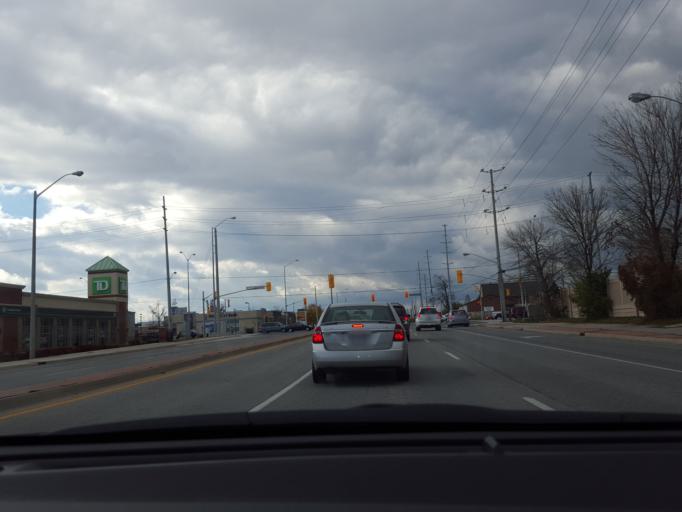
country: CA
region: Ontario
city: Brampton
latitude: 43.6672
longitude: -79.7806
